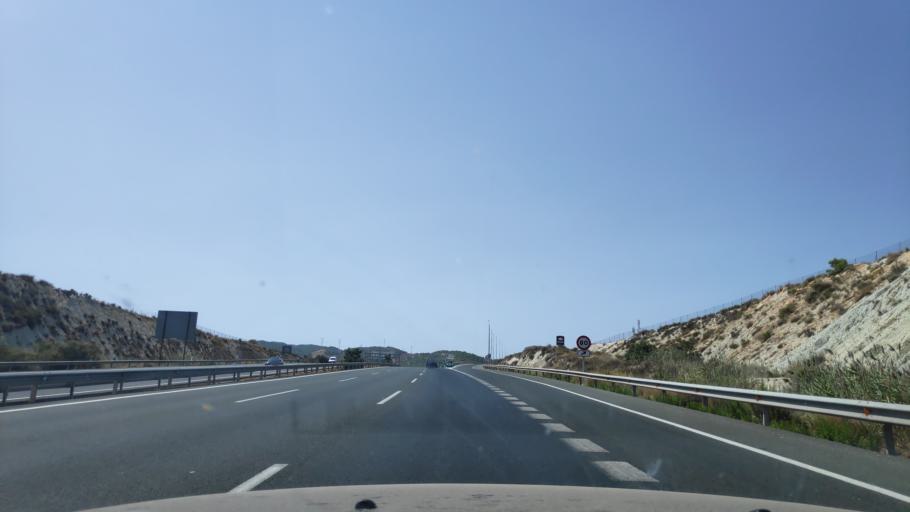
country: ES
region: Murcia
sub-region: Murcia
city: Murcia
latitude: 37.8812
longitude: -1.1329
